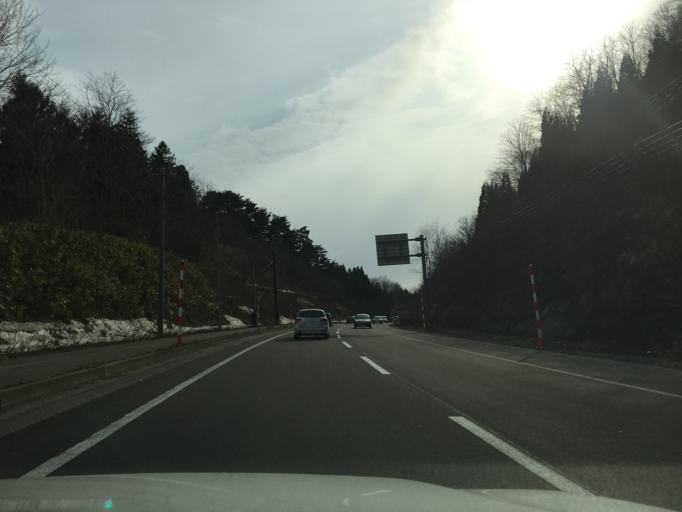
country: JP
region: Aomori
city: Namioka
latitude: 40.7714
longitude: 140.5980
